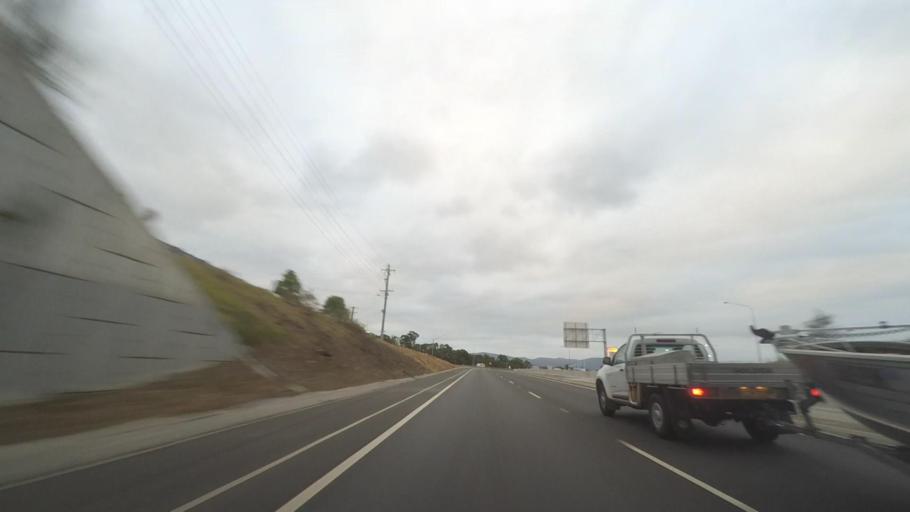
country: AU
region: New South Wales
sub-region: Shellharbour
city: Albion Park Rail
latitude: -34.5418
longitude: 150.7847
